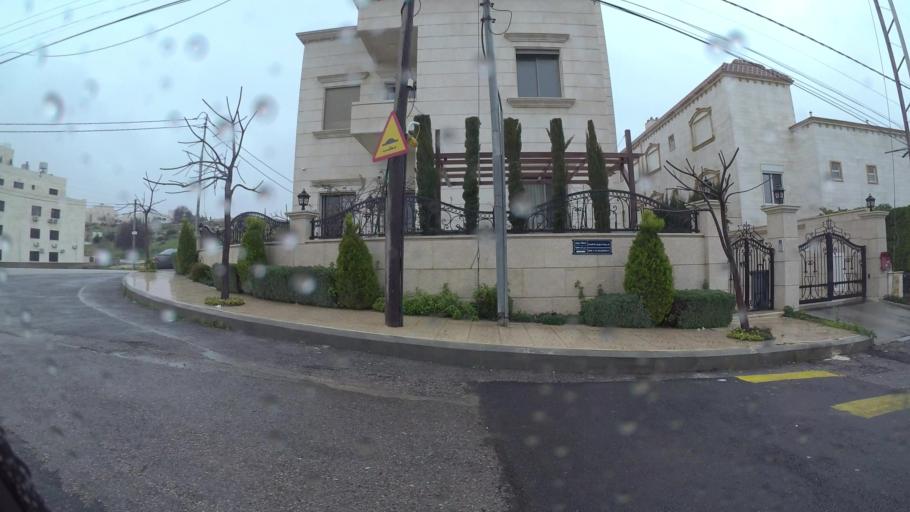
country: JO
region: Amman
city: Al Jubayhah
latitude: 32.0049
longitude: 35.8240
